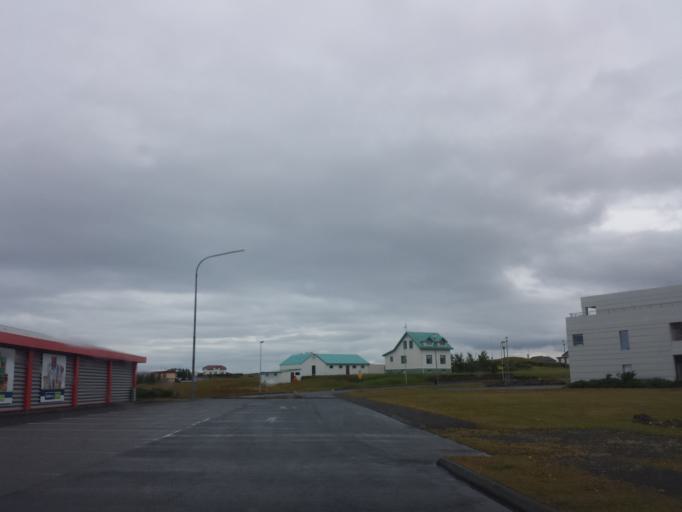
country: IS
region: Southern Peninsula
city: Sandgerdi
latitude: 64.0391
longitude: -22.7066
